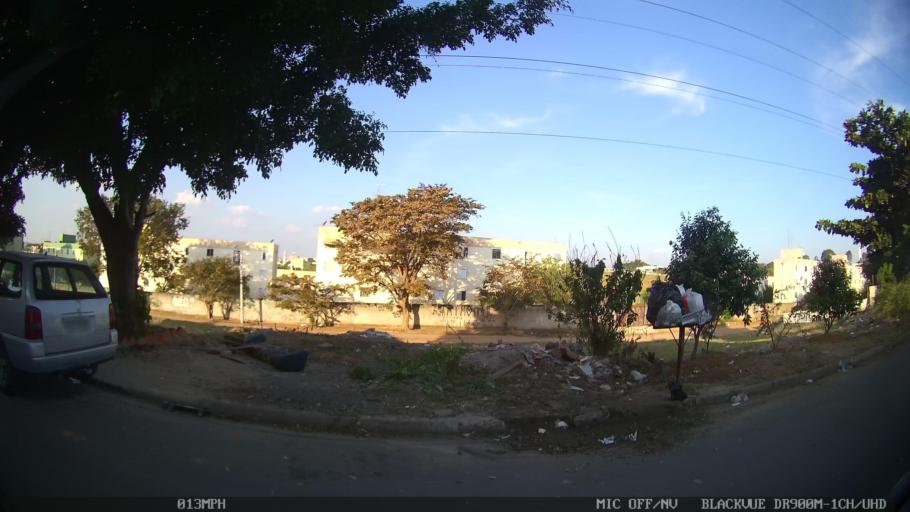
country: BR
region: Sao Paulo
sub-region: Campinas
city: Campinas
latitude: -22.9860
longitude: -47.1167
